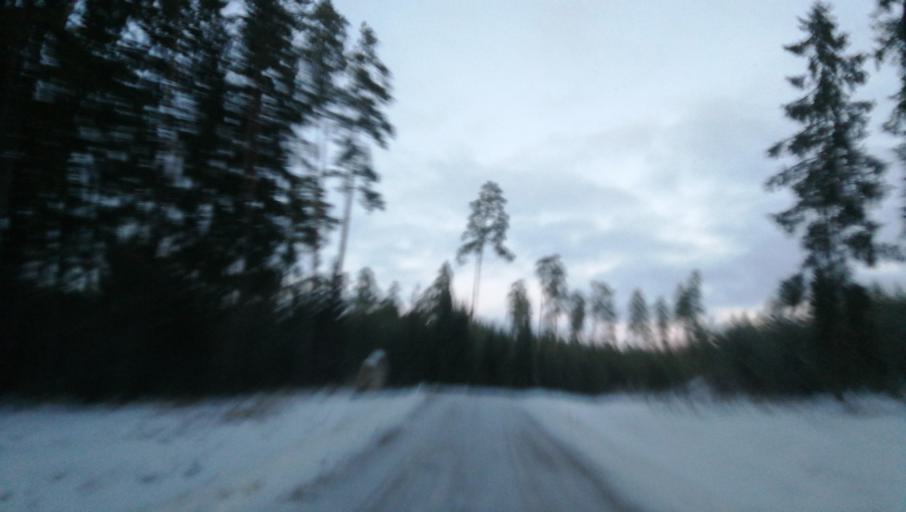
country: LV
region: Amatas Novads
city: Drabesi
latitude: 57.2140
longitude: 25.2832
